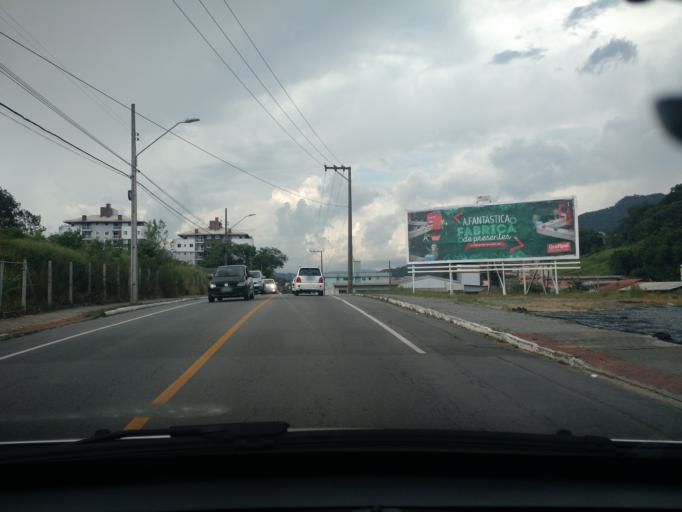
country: BR
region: Santa Catarina
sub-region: Jaragua Do Sul
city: Jaragua do Sul
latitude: -26.4902
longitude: -49.0914
